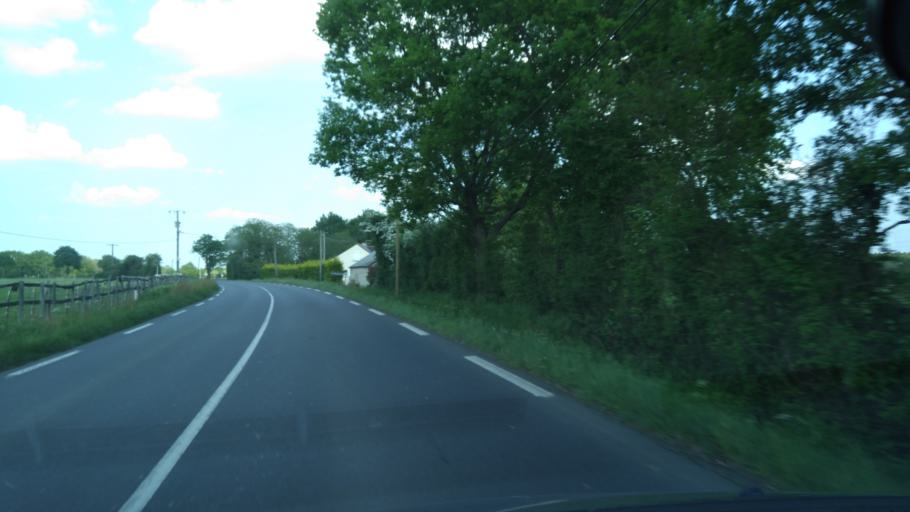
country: FR
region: Pays de la Loire
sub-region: Departement de la Loire-Atlantique
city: Heric
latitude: 47.4267
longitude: -1.6081
